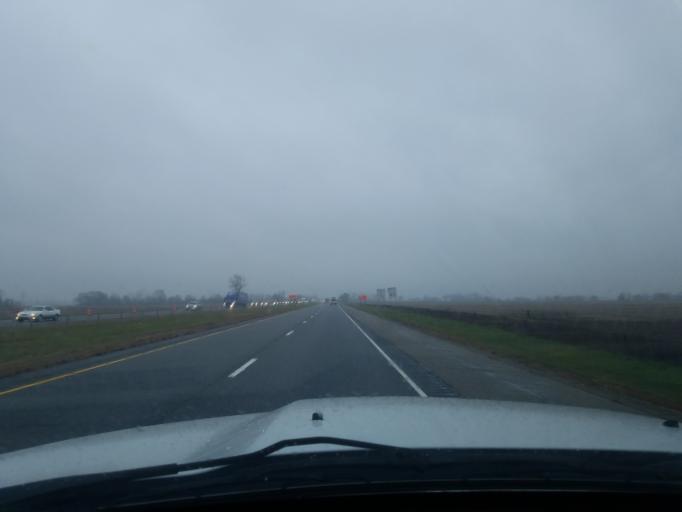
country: US
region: Indiana
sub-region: Grant County
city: Upland
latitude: 40.4155
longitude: -85.5494
